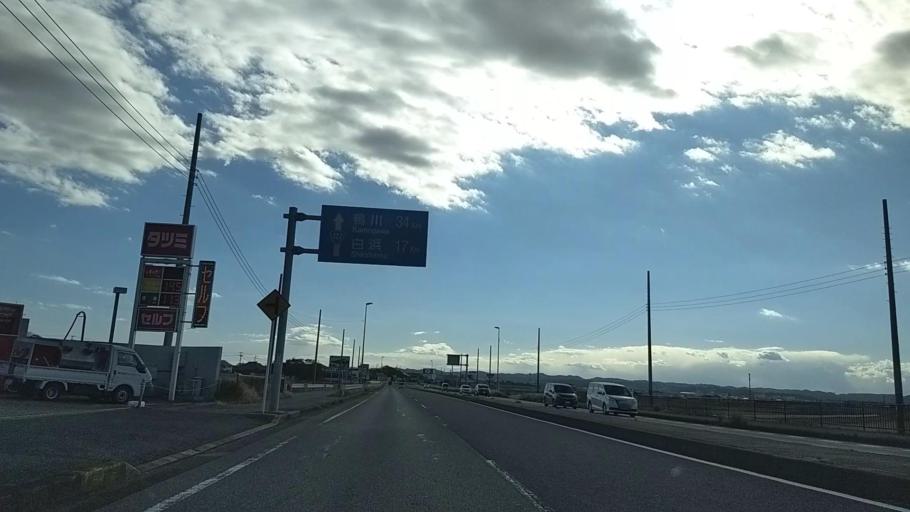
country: JP
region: Chiba
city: Tateyama
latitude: 35.0228
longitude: 139.8676
